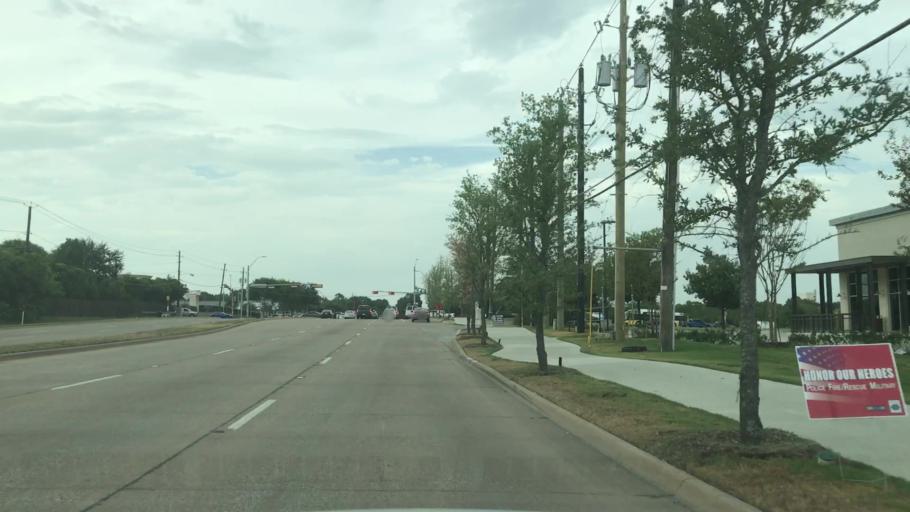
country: US
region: Texas
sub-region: Dallas County
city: University Park
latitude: 32.8772
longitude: -96.7348
